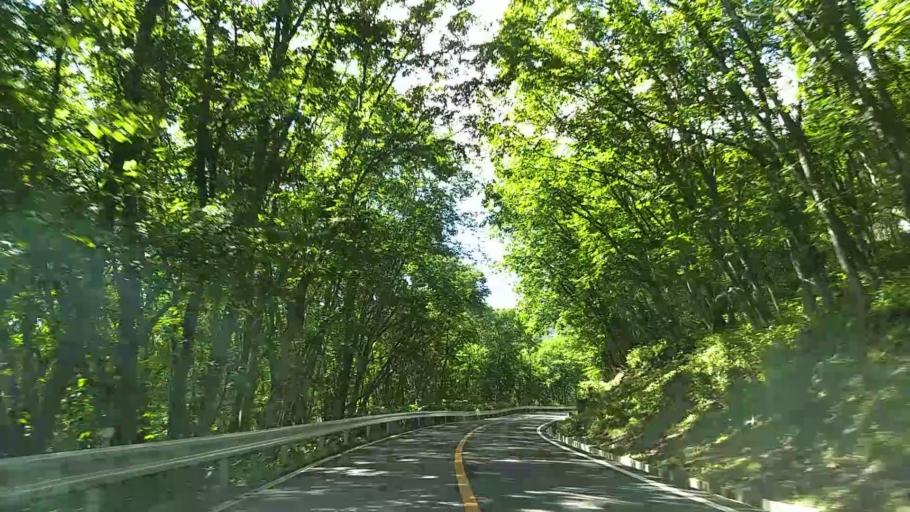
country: JP
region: Nagano
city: Chino
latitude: 36.0724
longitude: 138.2902
